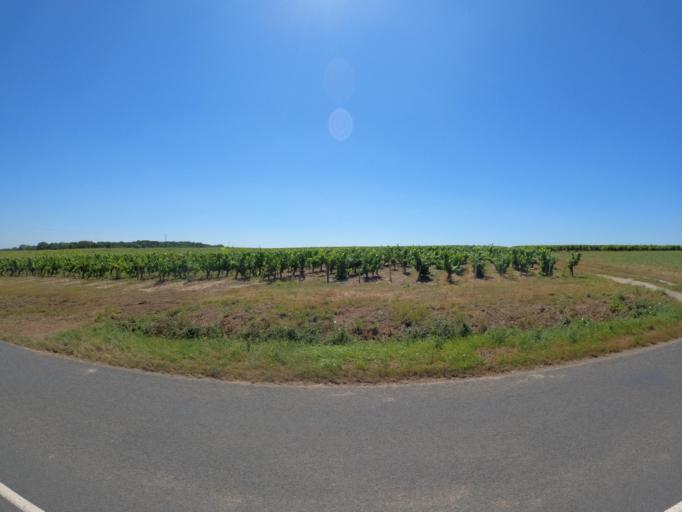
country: FR
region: Pays de la Loire
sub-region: Departement de la Loire-Atlantique
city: La Limouziniere
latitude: 46.9730
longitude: -1.5635
